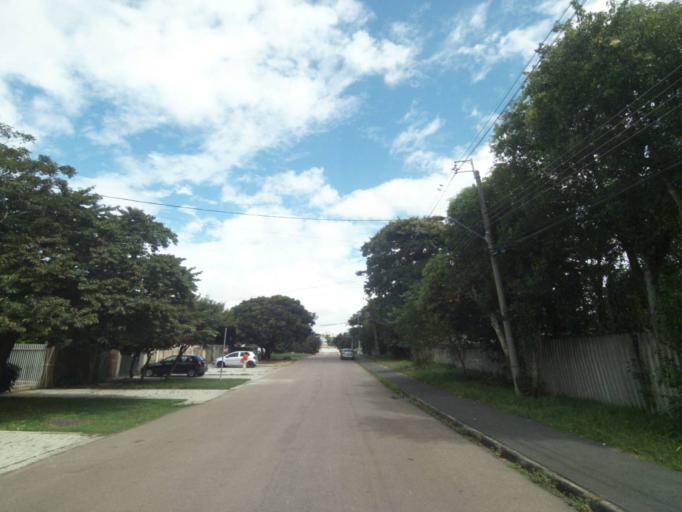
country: BR
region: Parana
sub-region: Curitiba
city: Curitiba
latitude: -25.4808
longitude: -49.2766
